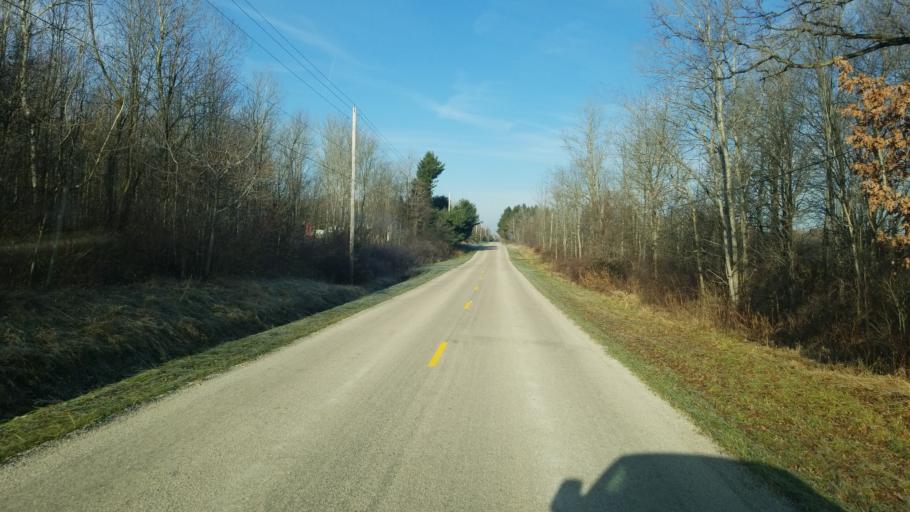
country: US
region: Ohio
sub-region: Ashtabula County
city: Andover
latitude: 41.6666
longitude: -80.6503
